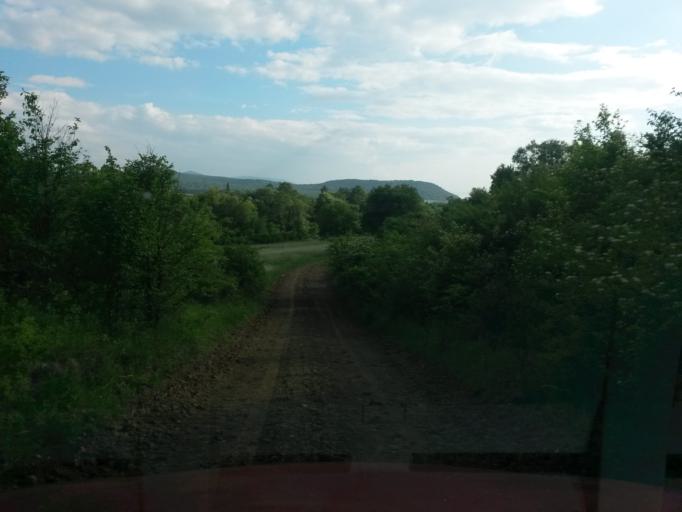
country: SK
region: Kosicky
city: Secovce
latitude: 48.7413
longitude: 21.4685
